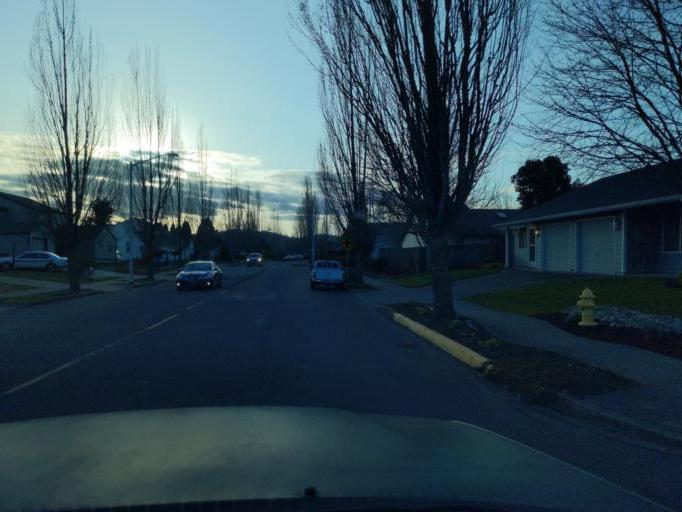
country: US
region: Oregon
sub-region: Yamhill County
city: McMinnville
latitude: 45.2018
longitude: -123.2244
